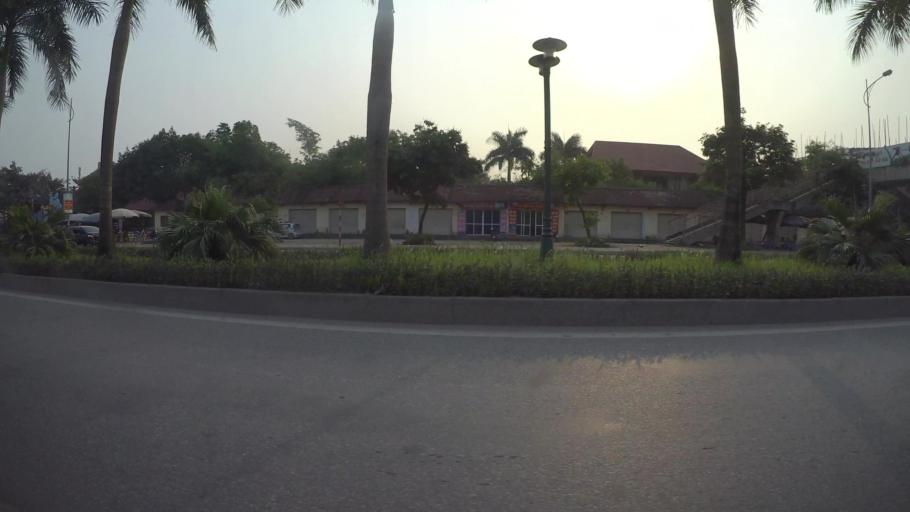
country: VN
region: Ha Noi
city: Cau Dien
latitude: 20.9997
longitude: 105.7339
